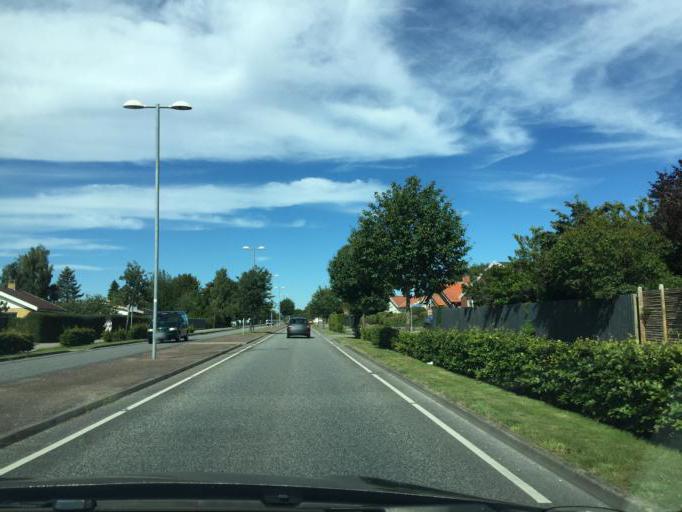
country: DK
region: Zealand
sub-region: Solrod Kommune
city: Solrod Strand
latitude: 55.5196
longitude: 12.2113
